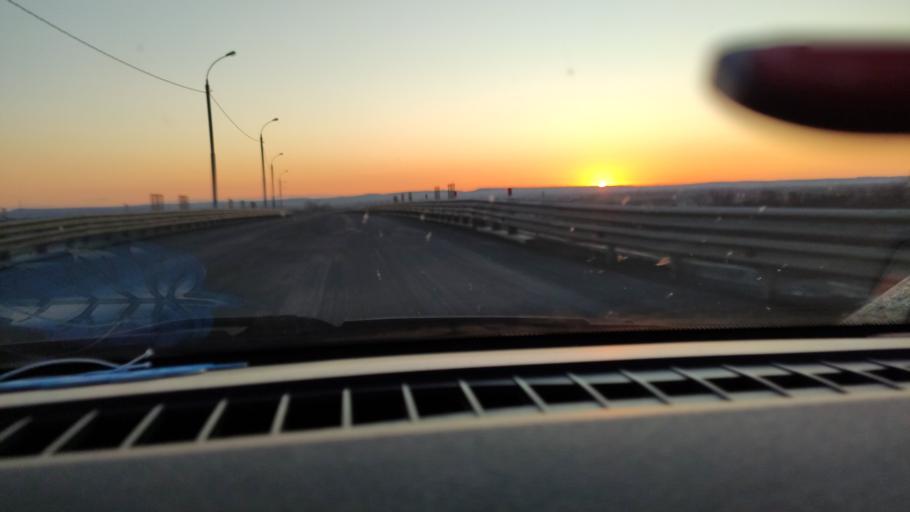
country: RU
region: Saratov
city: Yelshanka
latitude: 51.8005
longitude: 46.1870
